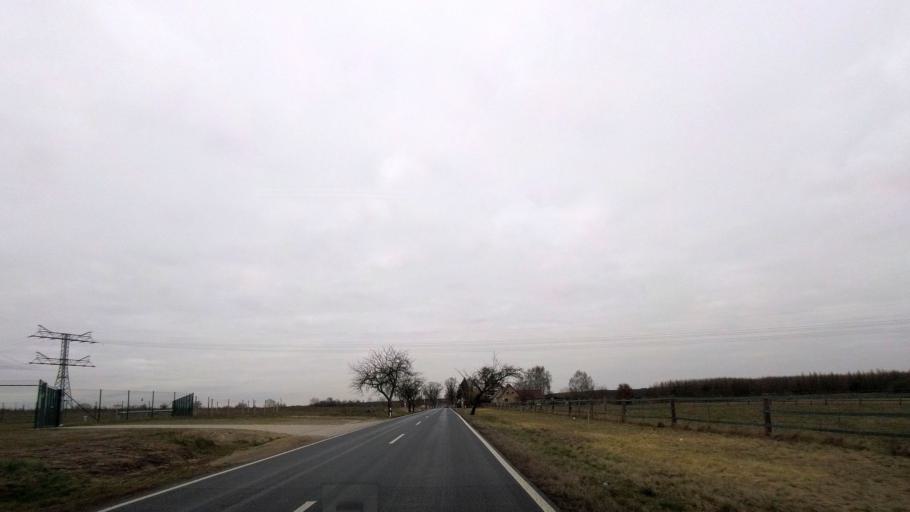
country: DE
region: Brandenburg
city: Treuenbrietzen
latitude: 52.1002
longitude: 12.8458
